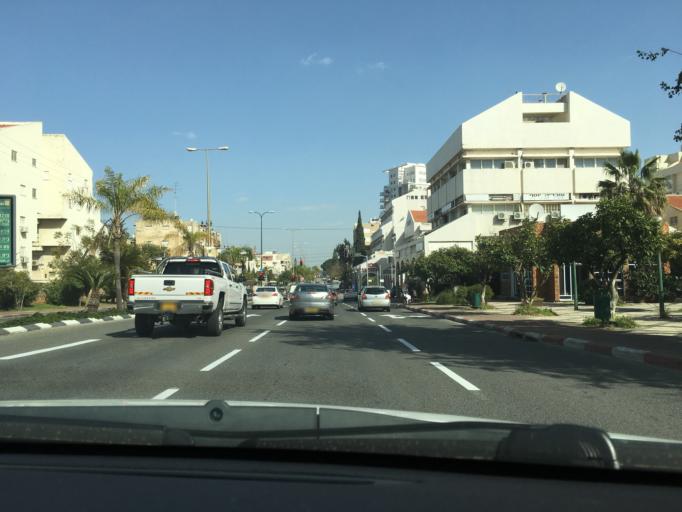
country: IL
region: Central District
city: Kfar Saba
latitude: 32.1763
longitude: 34.8925
